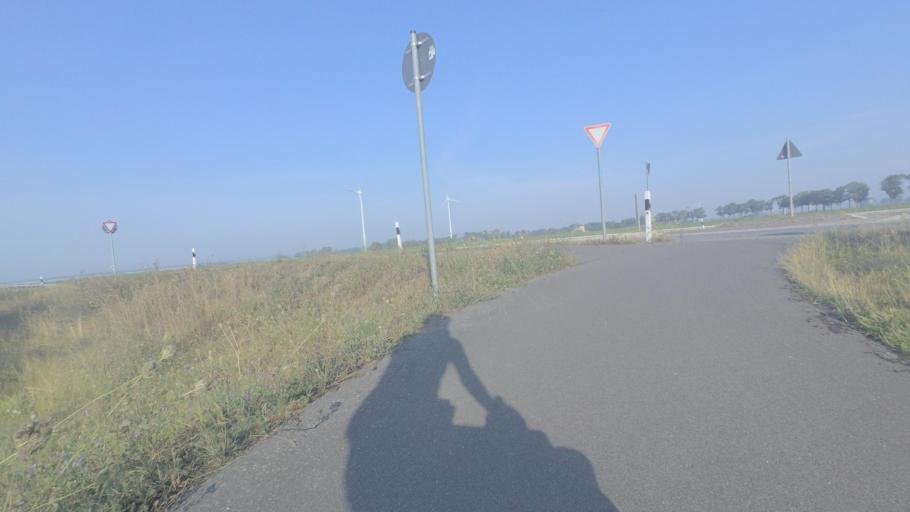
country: DE
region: Mecklenburg-Vorpommern
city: Gormin
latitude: 53.9946
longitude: 13.1475
